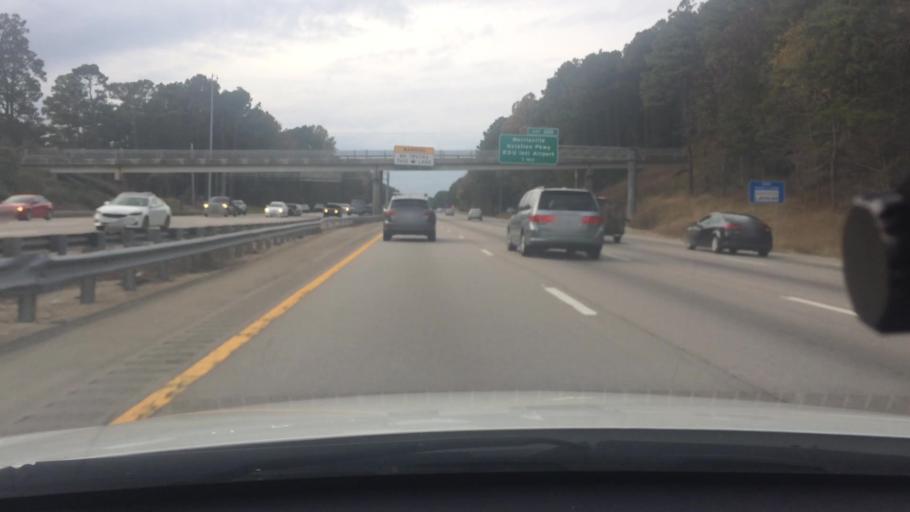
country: US
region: North Carolina
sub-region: Wake County
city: Morrisville
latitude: 35.8399
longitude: -78.7808
